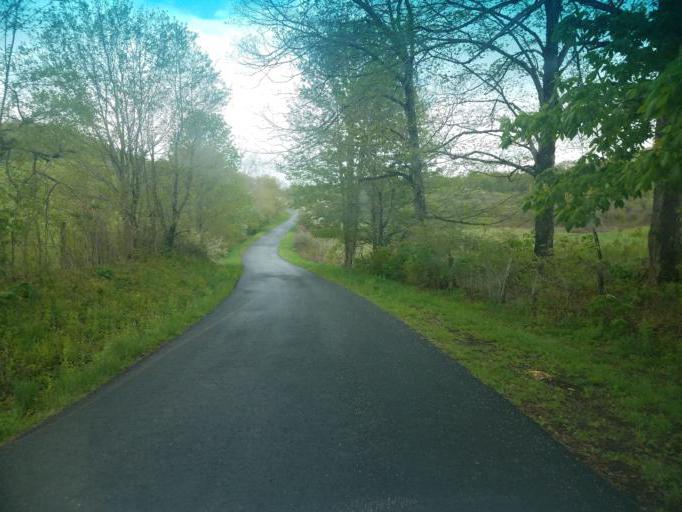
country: US
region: Virginia
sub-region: Smyth County
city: Atkins
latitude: 36.9583
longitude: -81.3953
